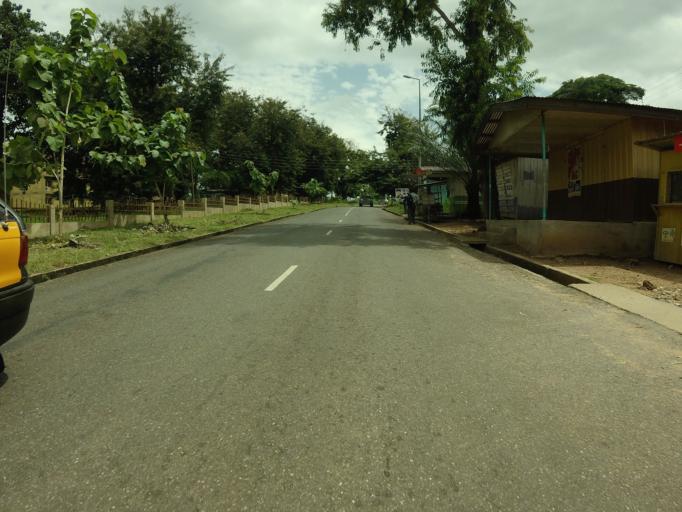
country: GH
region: Volta
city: Ho
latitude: 6.5923
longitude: 0.4691
